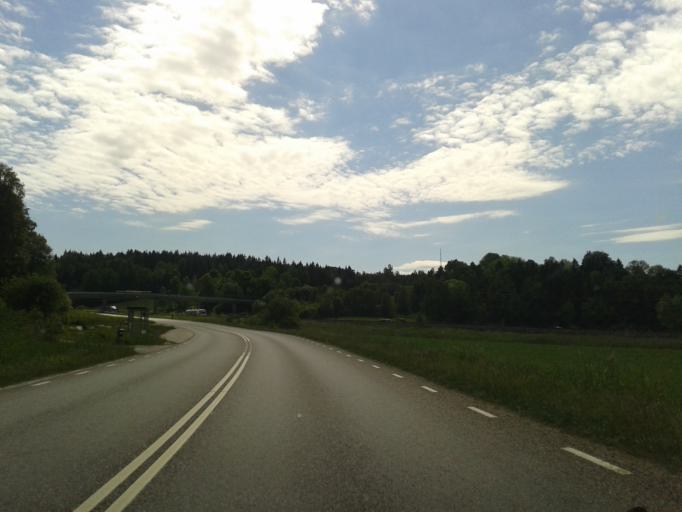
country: SE
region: Vaestra Goetaland
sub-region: Uddevalla Kommun
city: Ljungskile
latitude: 58.2778
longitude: 11.8875
